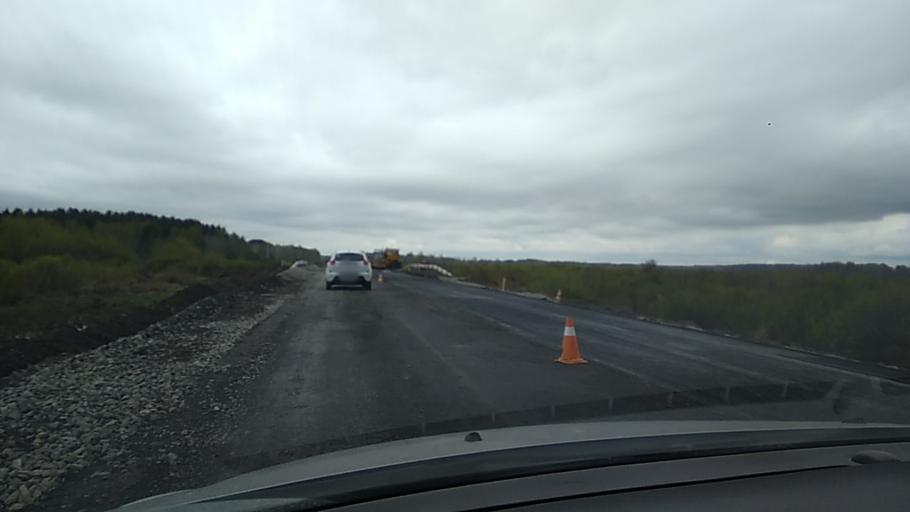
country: RU
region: Kurgan
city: Shadrinsk
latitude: 56.1532
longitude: 63.4205
